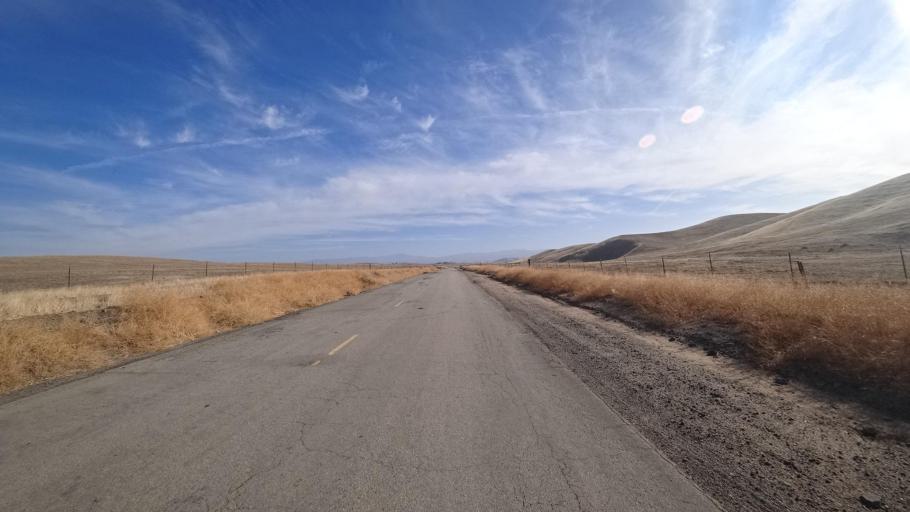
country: US
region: California
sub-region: Tulare County
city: Richgrove
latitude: 35.6235
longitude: -119.0051
